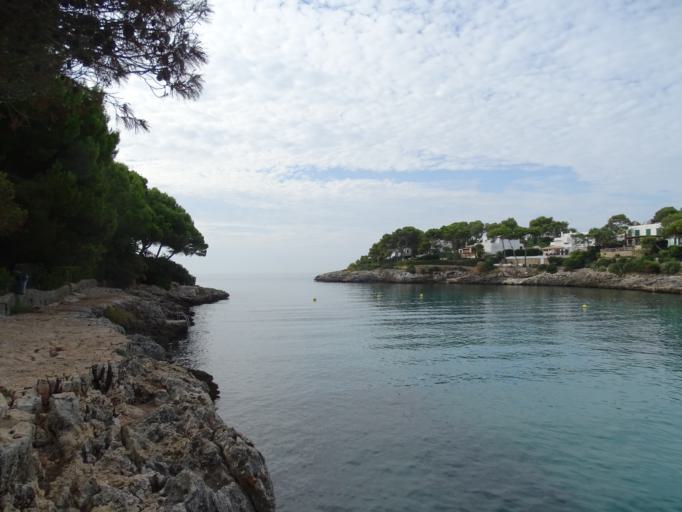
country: ES
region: Balearic Islands
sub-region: Illes Balears
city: Santanyi
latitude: 39.3727
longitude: 3.2334
